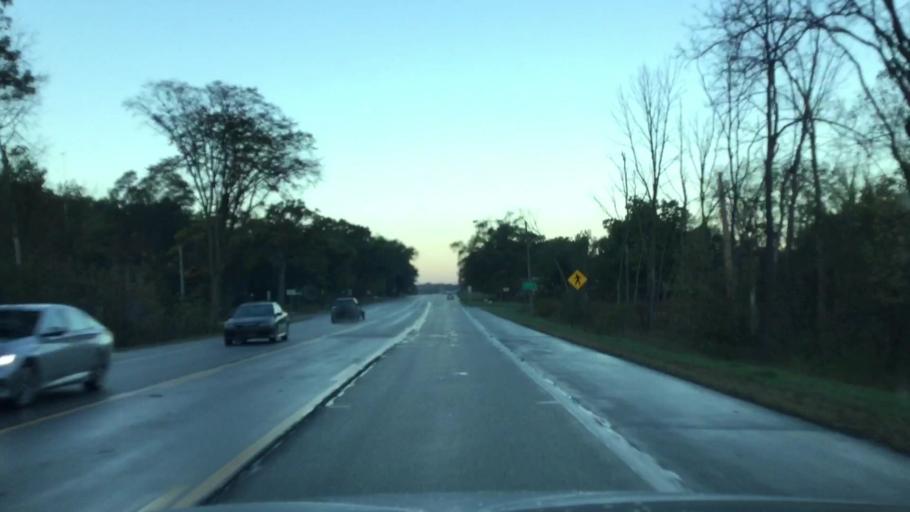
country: US
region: Michigan
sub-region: Livingston County
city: Howell
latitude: 42.6222
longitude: -83.9131
